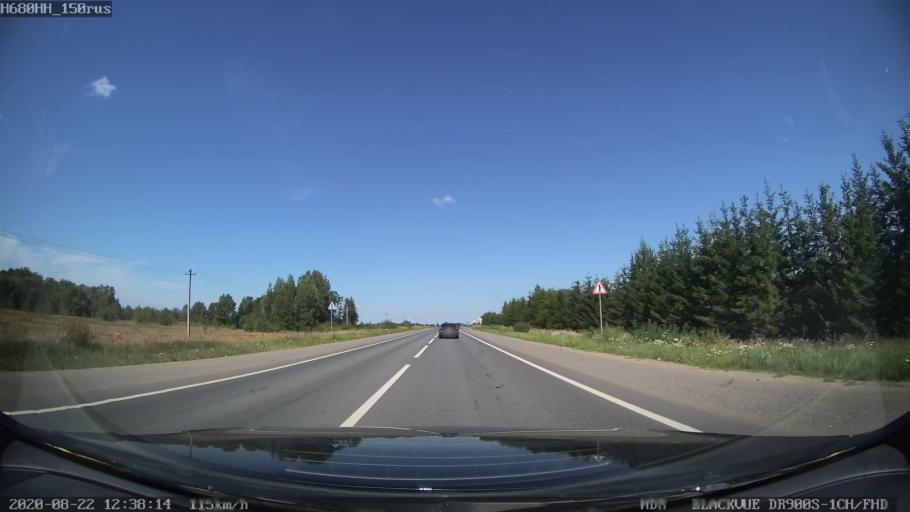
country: RU
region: Tverskaya
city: Rameshki
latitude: 57.3107
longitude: 36.0885
